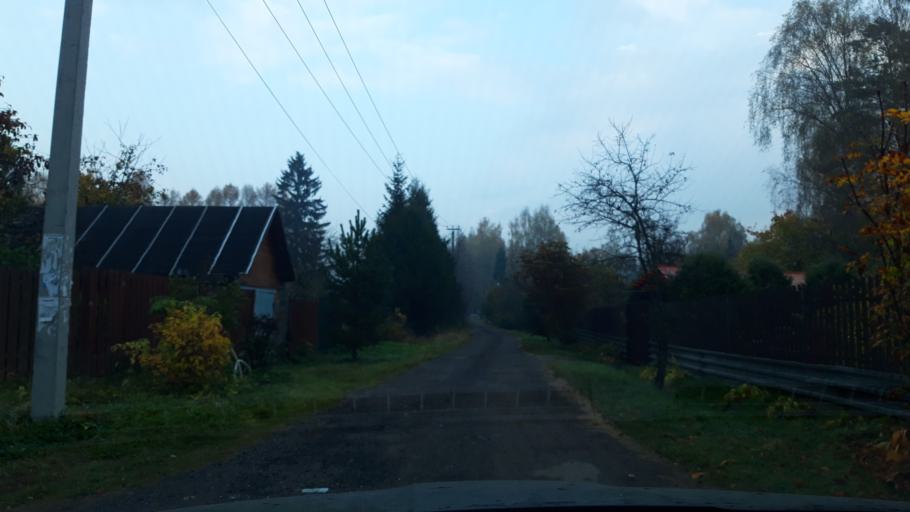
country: RU
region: Moskovskaya
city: Lozhki
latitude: 56.0526
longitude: 37.0972
